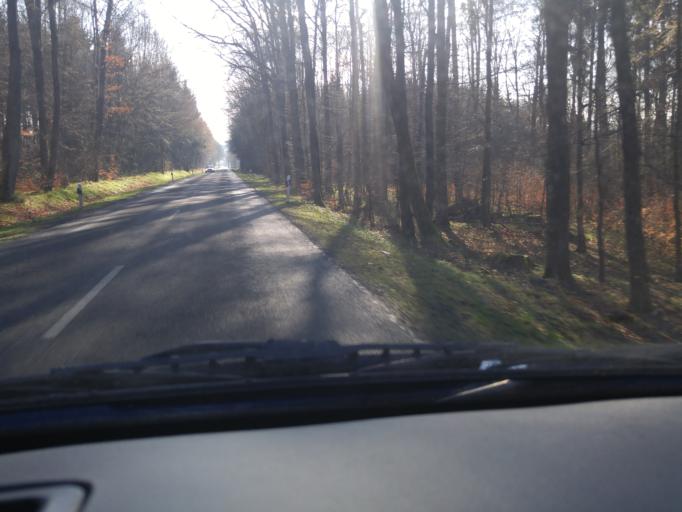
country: DE
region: Hesse
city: Herbstein
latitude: 50.5825
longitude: 9.3478
